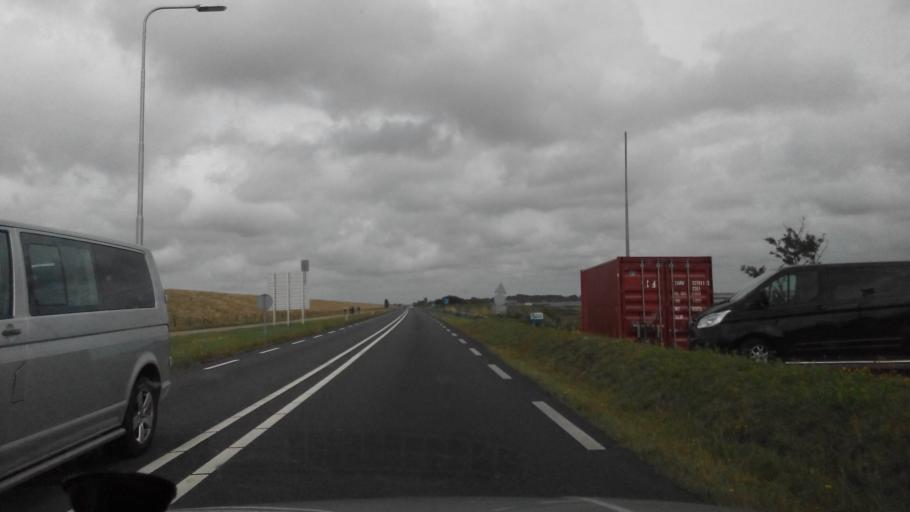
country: NL
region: North Holland
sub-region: Gemeente Schagen
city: Schagen
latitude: 52.8869
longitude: 4.8756
